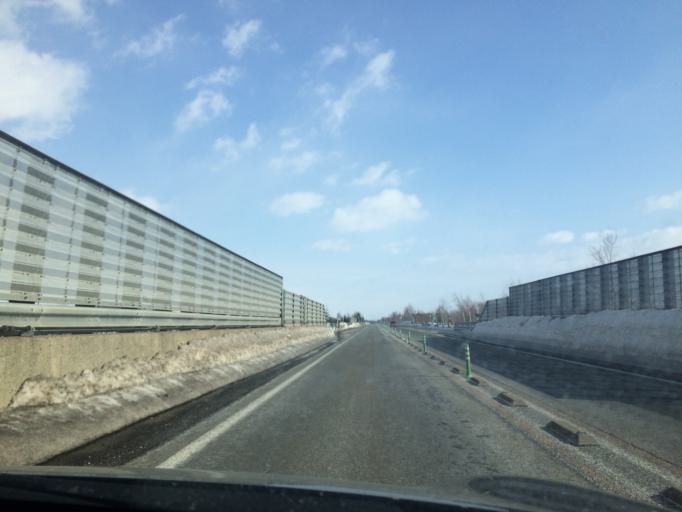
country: JP
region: Hokkaido
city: Chitose
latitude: 42.8640
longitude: 141.6084
